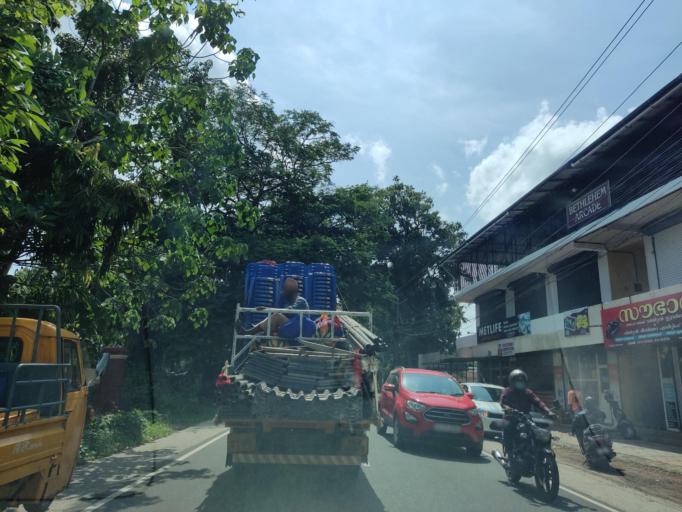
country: IN
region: Kerala
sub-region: Alappuzha
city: Mavelikara
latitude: 9.2679
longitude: 76.5401
